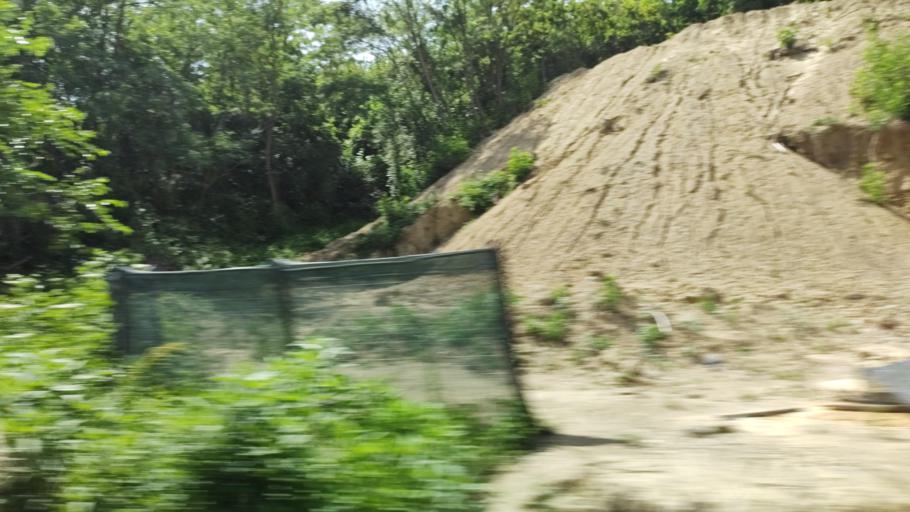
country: RO
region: Mehedinti
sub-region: Comuna Eselnita
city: Eselnita
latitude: 44.6867
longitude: 22.3622
